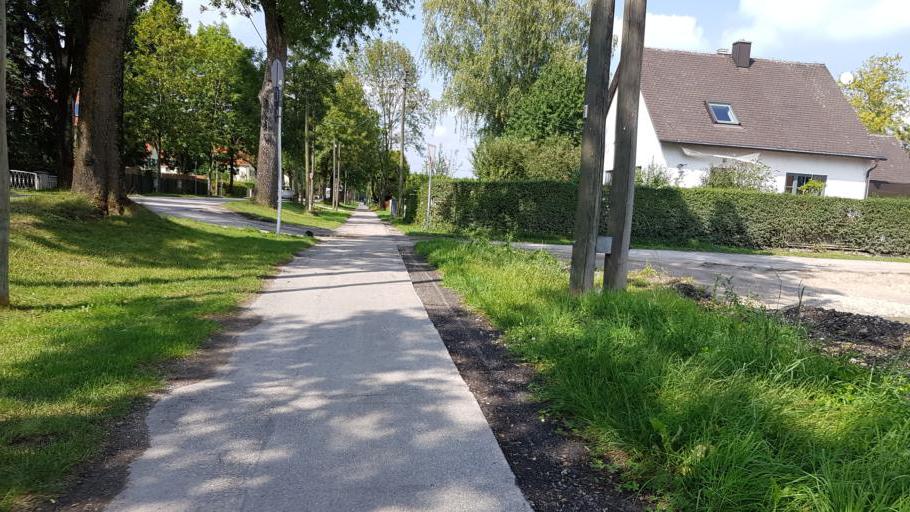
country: DE
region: Bavaria
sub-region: Upper Bavaria
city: Karlsfeld
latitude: 48.2040
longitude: 11.4933
